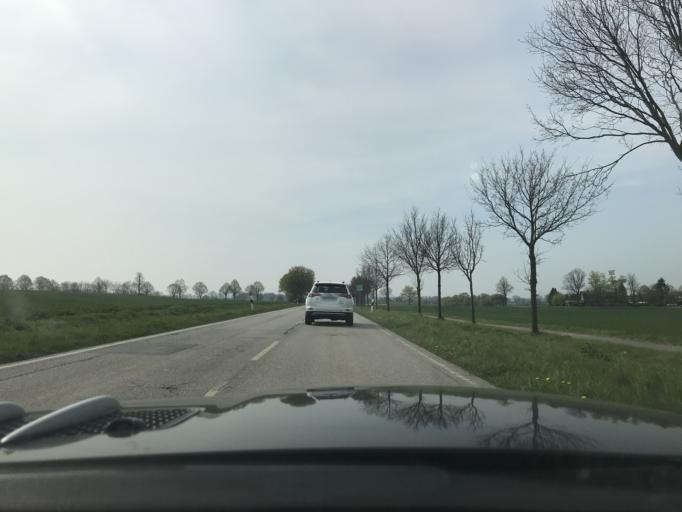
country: DE
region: Schleswig-Holstein
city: Grube
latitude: 54.2680
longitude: 11.0338
